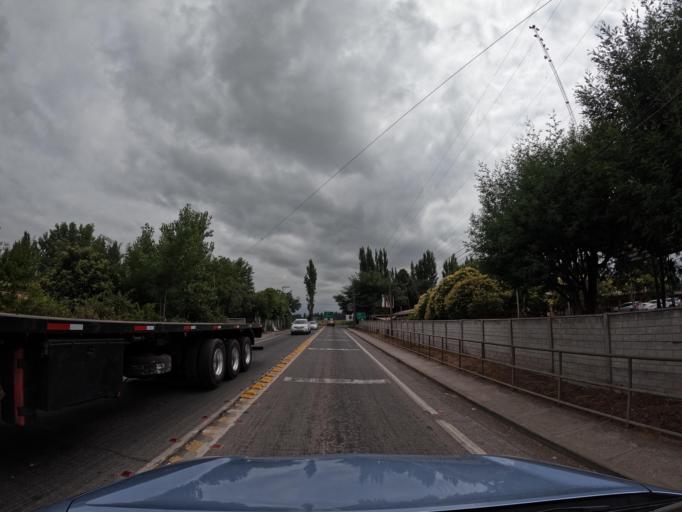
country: CL
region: Maule
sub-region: Provincia de Curico
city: Teno
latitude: -34.7501
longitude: -71.2383
